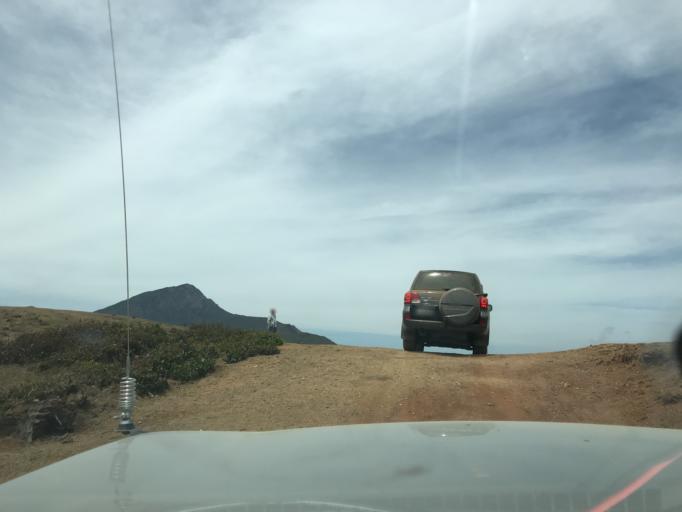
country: TL
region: Ainaro
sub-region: Ainaro
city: Ainaro
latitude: -8.8736
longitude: 125.5221
